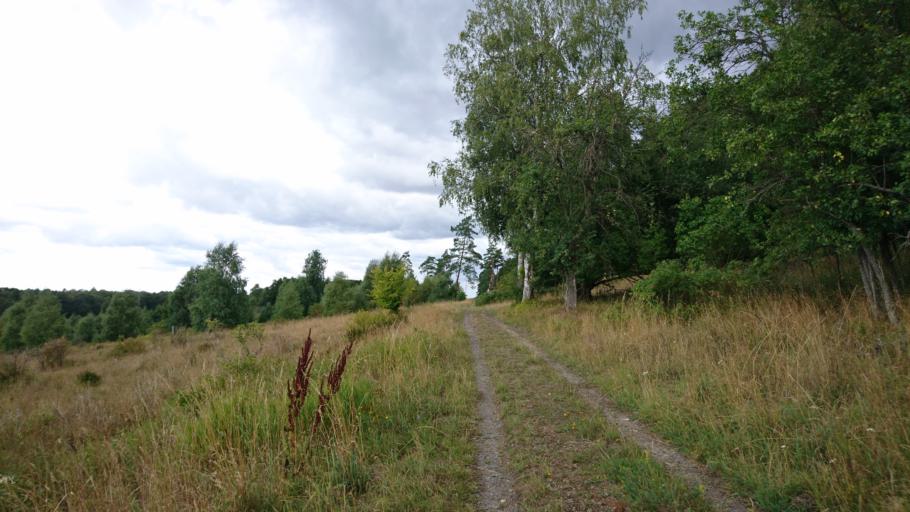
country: SE
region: Skane
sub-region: Sjobo Kommun
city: Sjoebo
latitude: 55.5920
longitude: 13.7712
